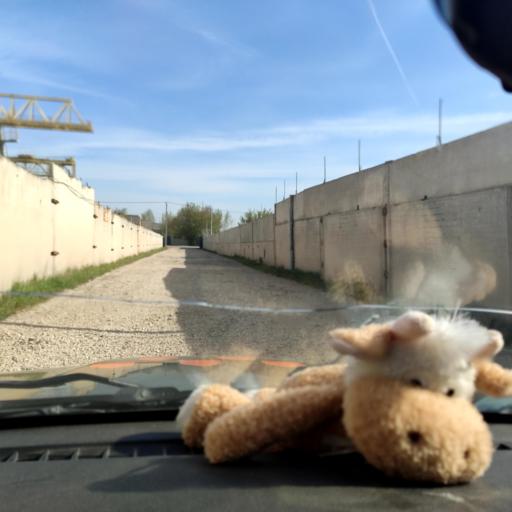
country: RU
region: Samara
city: Tol'yatti
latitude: 53.5749
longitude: 49.2755
